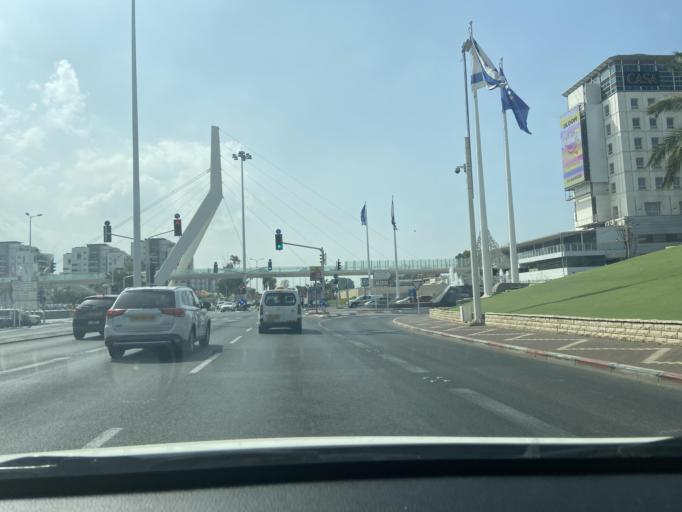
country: IL
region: Northern District
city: Nahariya
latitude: 33.0064
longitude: 35.0995
